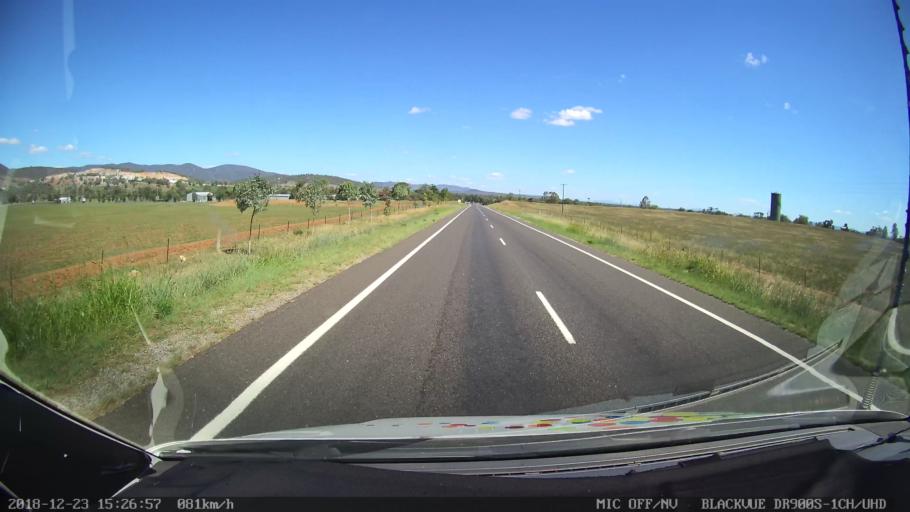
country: AU
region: New South Wales
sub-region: Tamworth Municipality
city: East Tamworth
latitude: -30.9228
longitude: 150.8422
